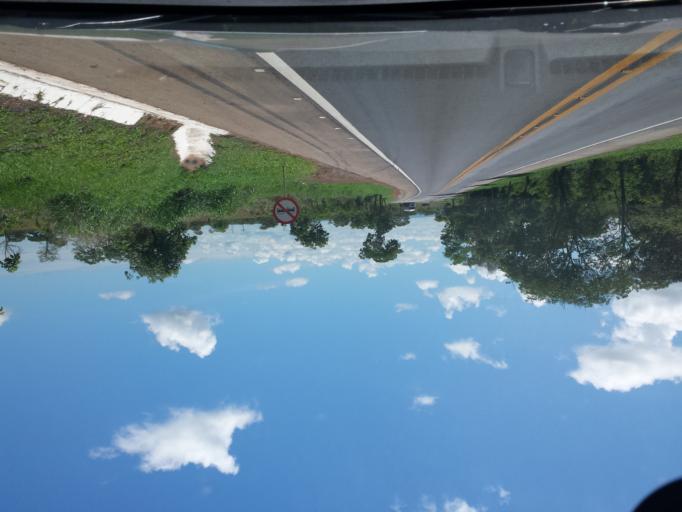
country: BR
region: Goias
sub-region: Luziania
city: Luziania
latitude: -16.3647
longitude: -47.8282
